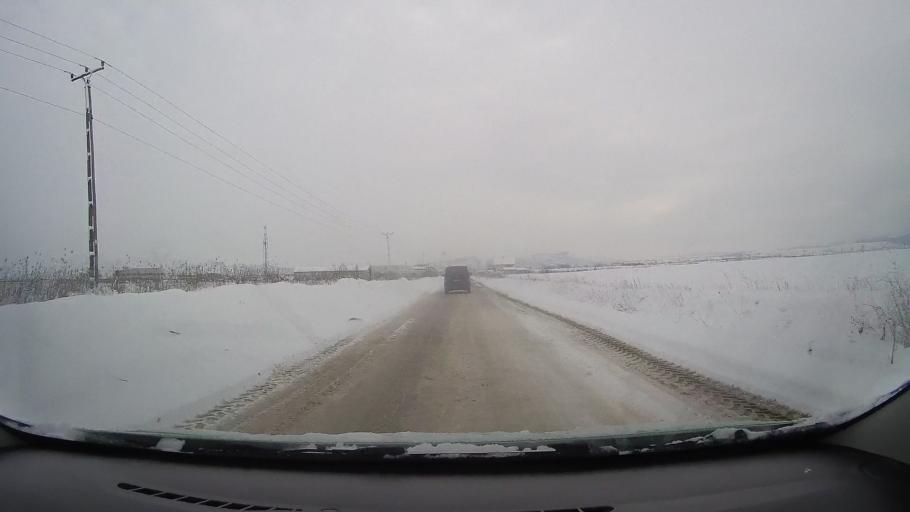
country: RO
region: Alba
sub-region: Municipiul Sebes
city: Lancram
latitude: 45.9601
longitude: 23.5317
